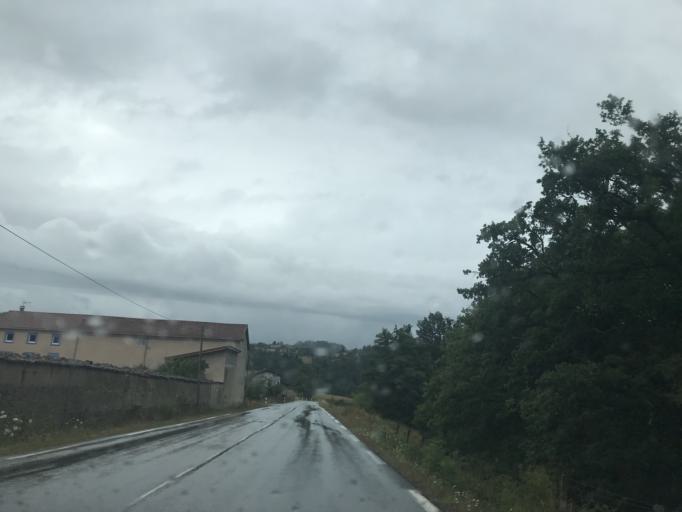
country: FR
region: Auvergne
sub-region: Departement du Puy-de-Dome
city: Job
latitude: 45.5832
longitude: 3.7334
